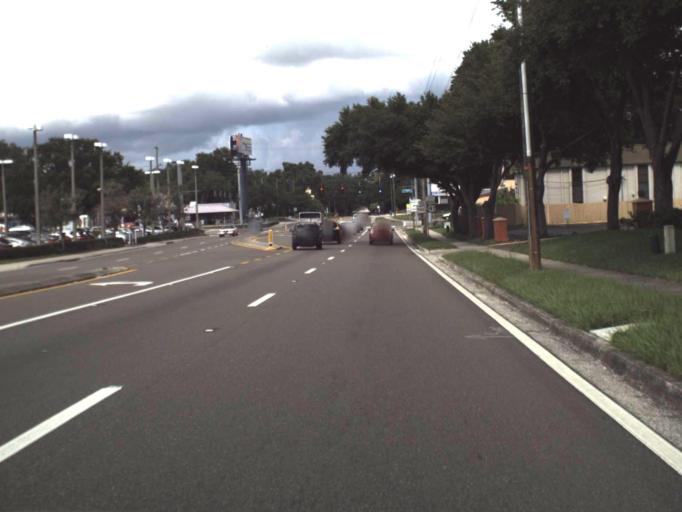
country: US
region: Florida
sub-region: Hillsborough County
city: Lake Magdalene
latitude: 28.0547
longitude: -82.4577
